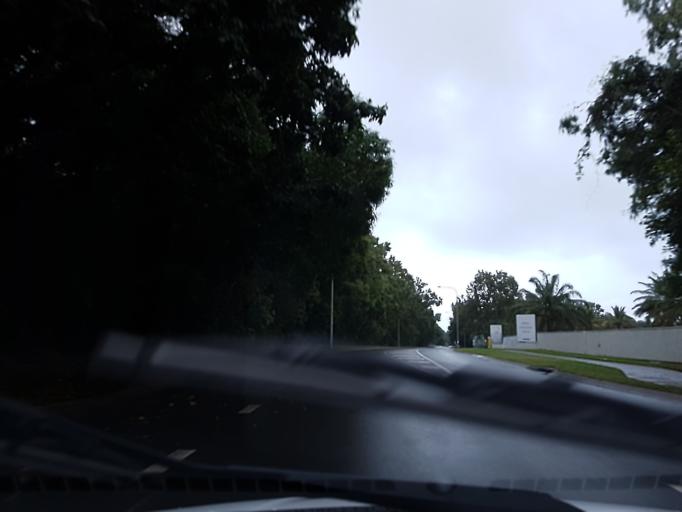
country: AU
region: Queensland
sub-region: Cairns
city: Palm Cove
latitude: -16.7543
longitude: 145.6658
